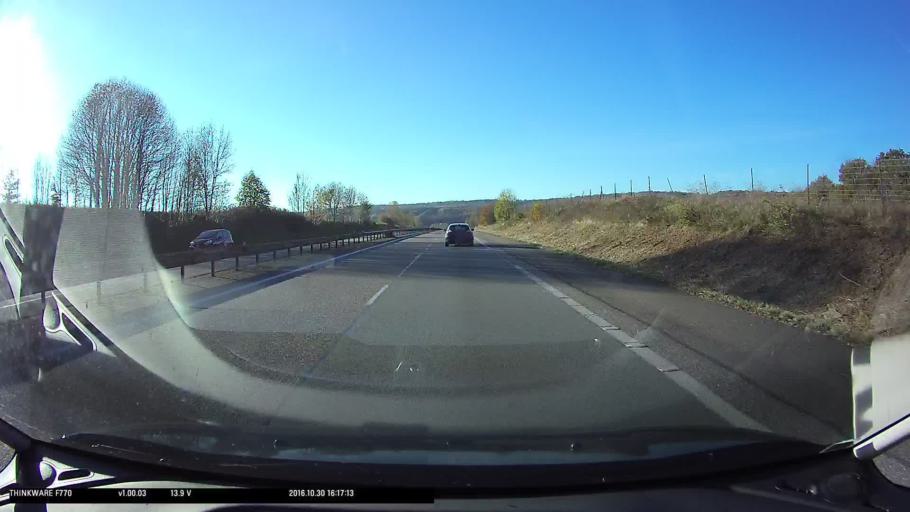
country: FR
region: Franche-Comte
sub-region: Departement du Doubs
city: Clerval
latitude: 47.4106
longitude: 6.5271
